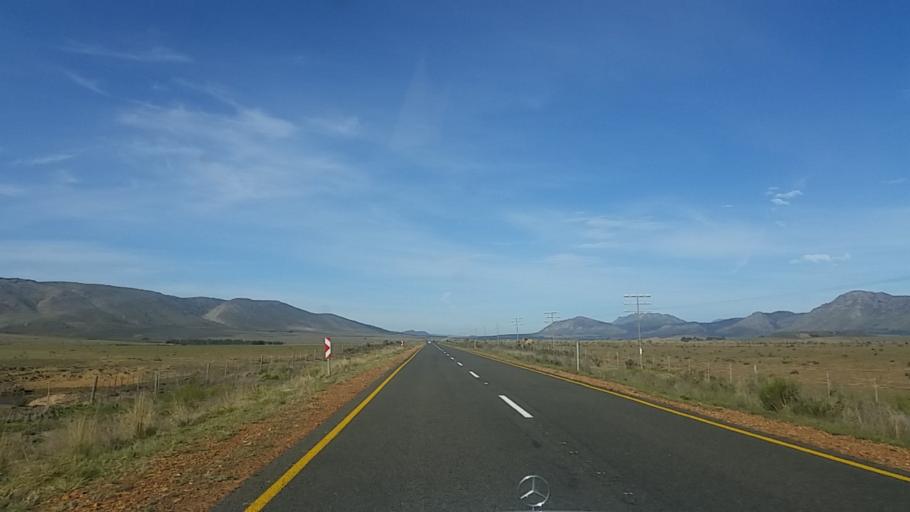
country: ZA
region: Western Cape
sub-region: Eden District Municipality
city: George
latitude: -33.8125
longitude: 22.5317
